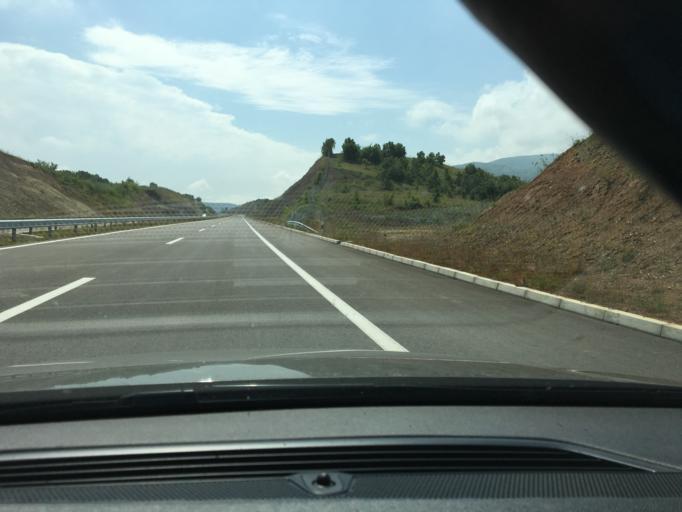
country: MK
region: Petrovec
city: Sredno Konjare
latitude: 41.9545
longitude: 21.7505
